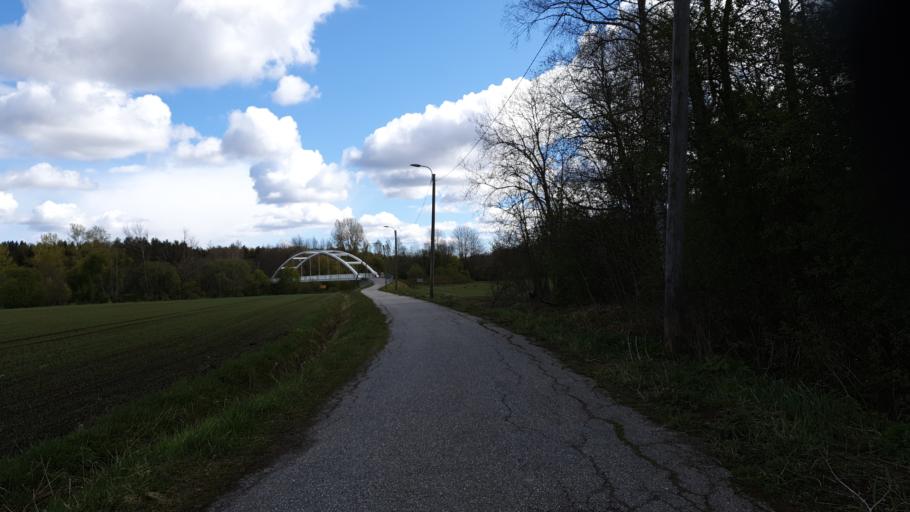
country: FI
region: Uusimaa
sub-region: Helsinki
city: Nurmijaervi
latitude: 60.3399
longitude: 24.8279
